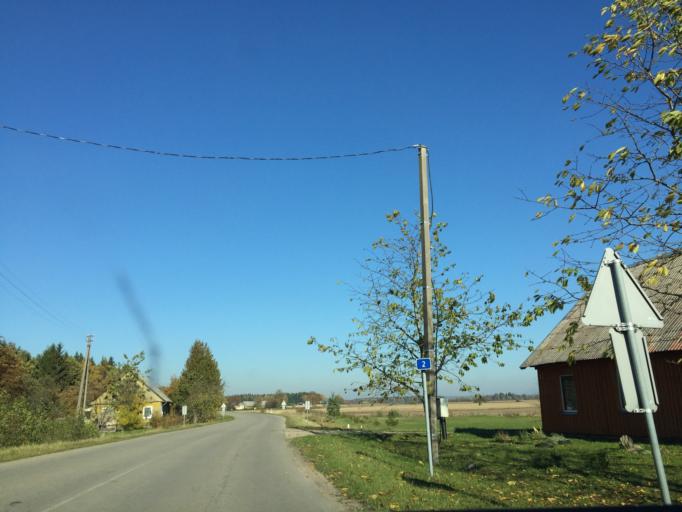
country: LT
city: Salantai
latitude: 55.9604
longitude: 21.6518
